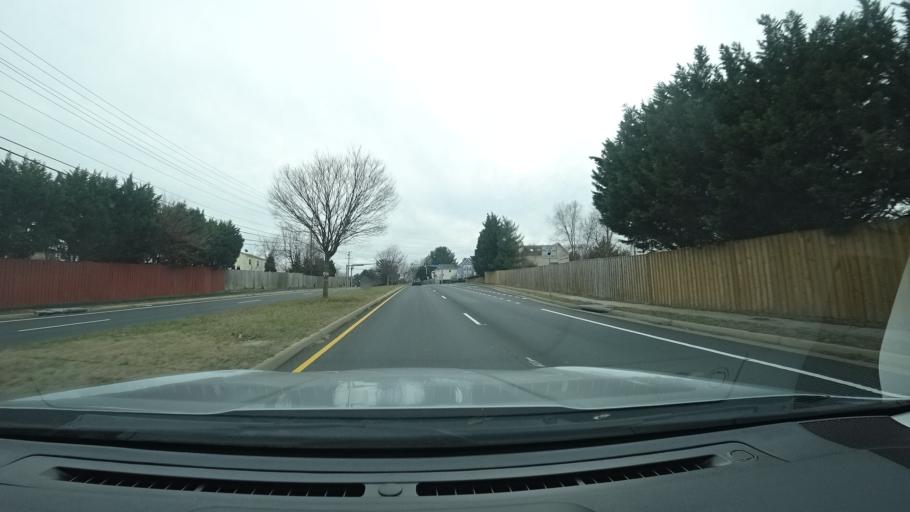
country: US
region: Virginia
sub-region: Fairfax County
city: Dranesville
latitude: 39.0006
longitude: -77.3764
